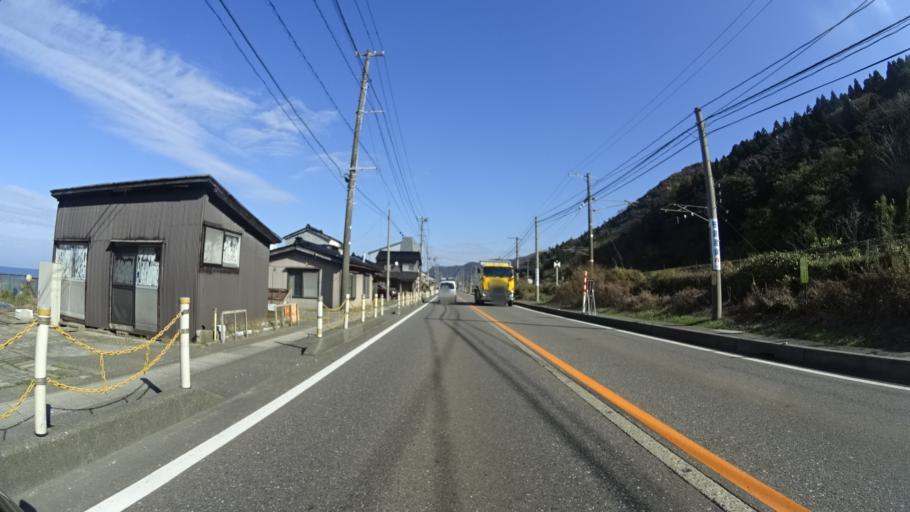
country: JP
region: Niigata
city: Itoigawa
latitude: 37.0618
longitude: 137.9162
